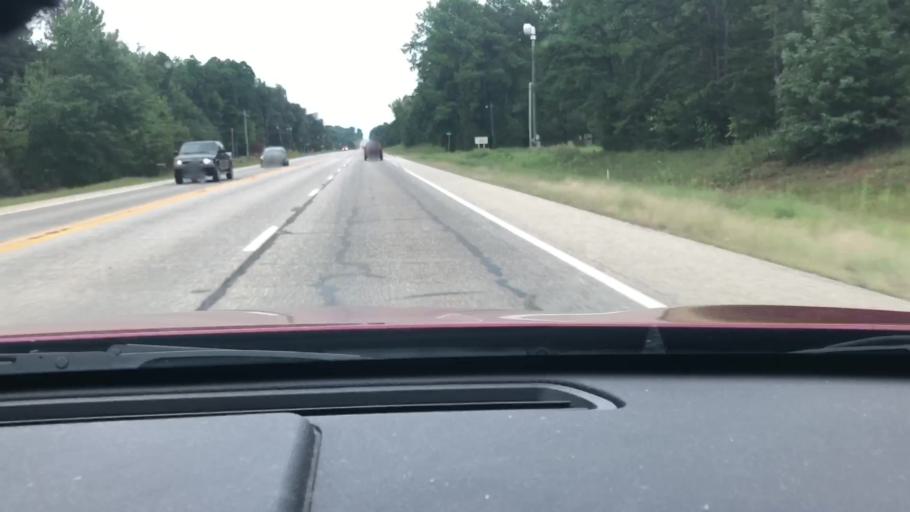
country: US
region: Arkansas
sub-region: Miller County
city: Texarkana
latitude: 33.4296
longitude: -93.9573
